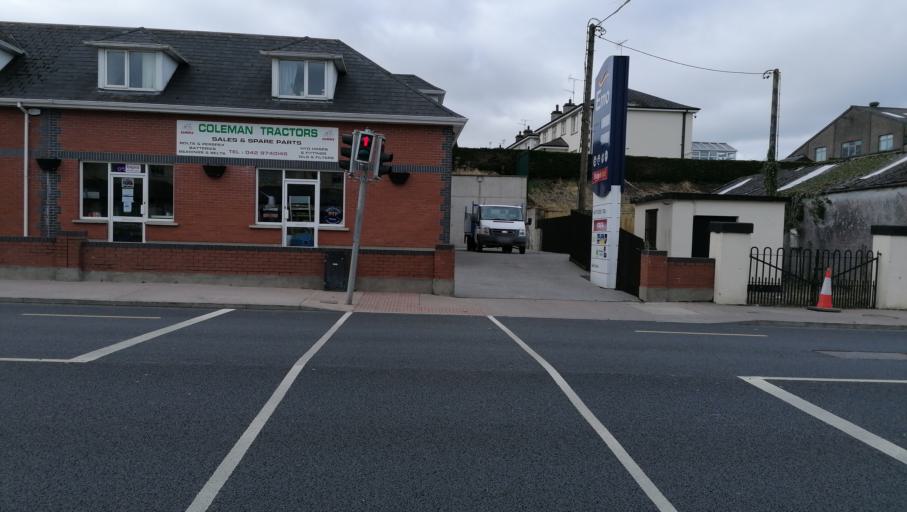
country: IE
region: Ulster
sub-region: County Monaghan
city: Castleblayney
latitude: 54.1210
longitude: -6.7405
